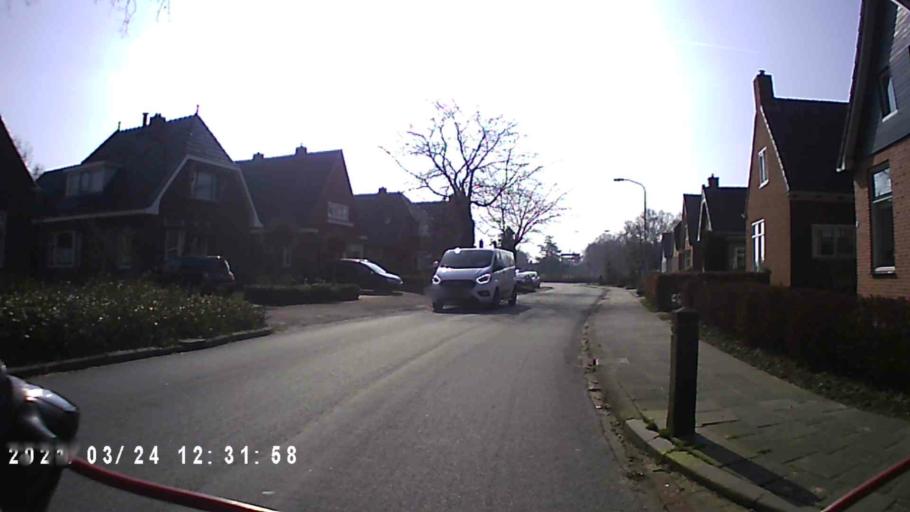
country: NL
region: Groningen
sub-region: Gemeente Leek
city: Leek
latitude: 53.1723
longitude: 6.3638
